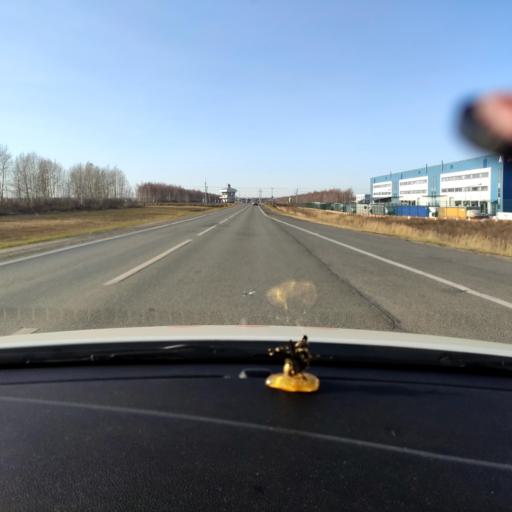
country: RU
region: Tatarstan
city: Stolbishchi
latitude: 55.6327
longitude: 49.2544
